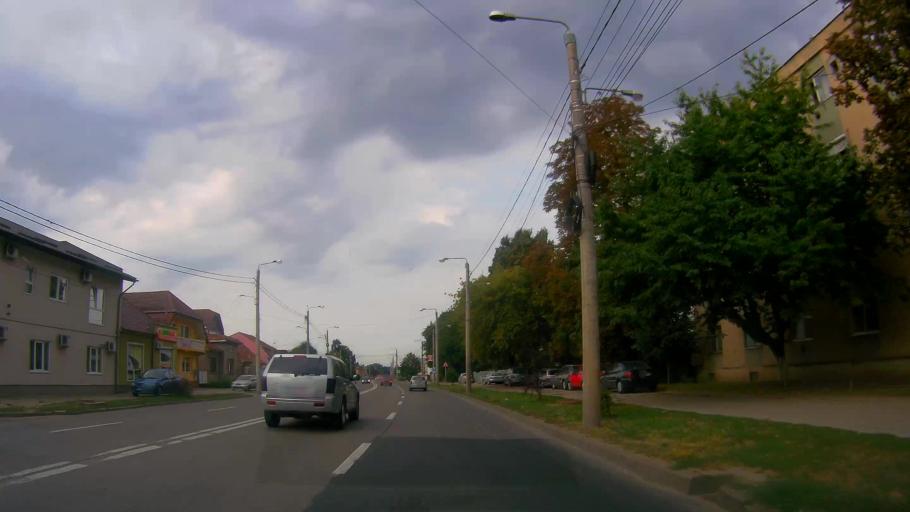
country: RO
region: Satu Mare
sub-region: Municipiul Satu Mare
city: Satu Mare
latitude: 47.7946
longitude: 22.8942
